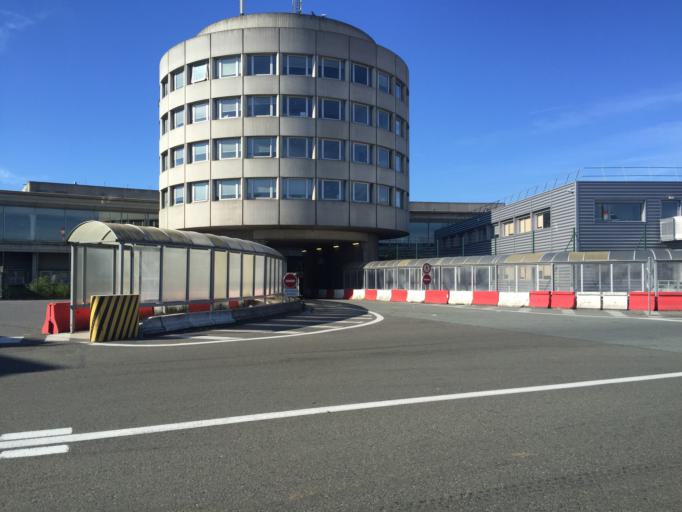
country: FR
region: Ile-de-France
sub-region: Departement du Val-d'Oise
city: Roissy-en-France
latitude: 49.0047
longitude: 2.5649
